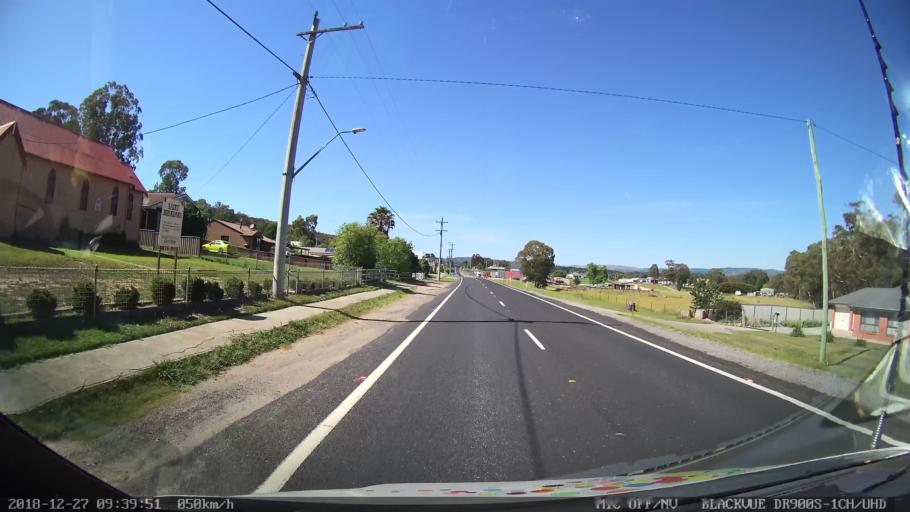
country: AU
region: New South Wales
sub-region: Lithgow
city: Portland
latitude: -33.2963
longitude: 150.0340
